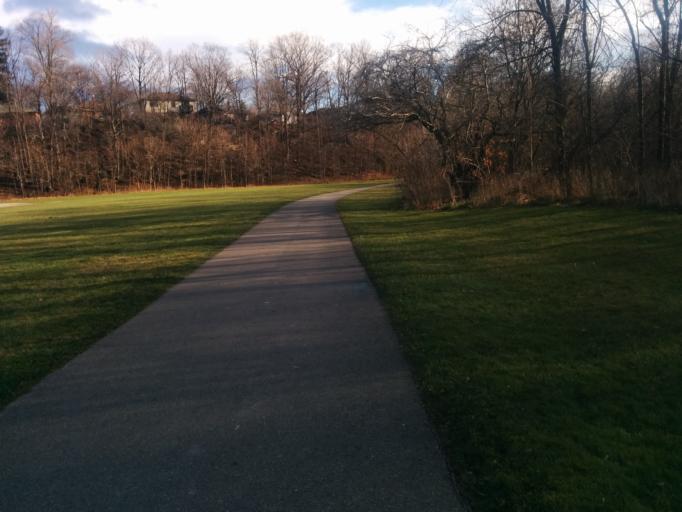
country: CA
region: Ontario
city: Etobicoke
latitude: 43.6035
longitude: -79.5571
